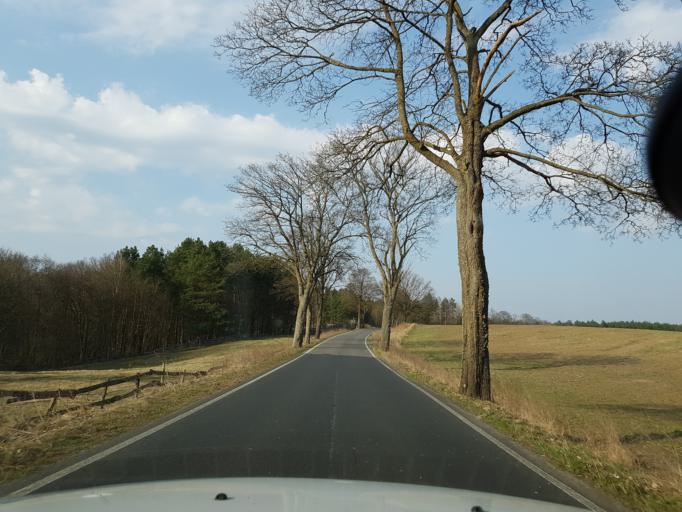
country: PL
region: West Pomeranian Voivodeship
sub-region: Powiat drawski
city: Zlocieniec
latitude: 53.6122
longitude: 15.9212
